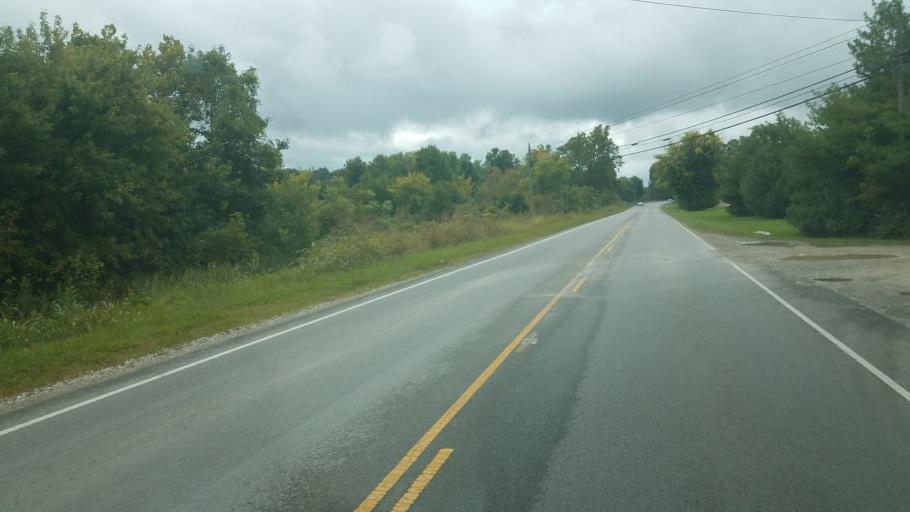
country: US
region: Ohio
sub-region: Scioto County
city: Wheelersburg
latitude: 38.7044
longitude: -82.8543
